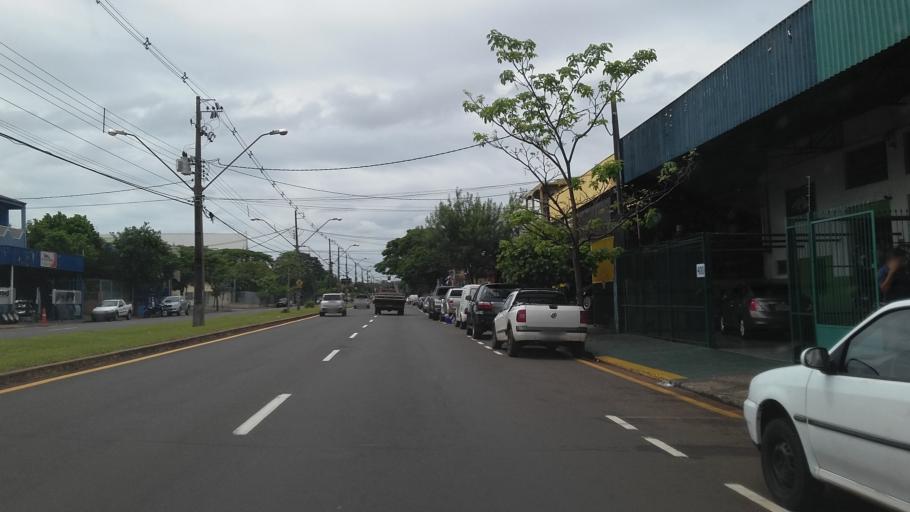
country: BR
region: Parana
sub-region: Londrina
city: Londrina
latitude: -23.2965
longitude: -51.1458
